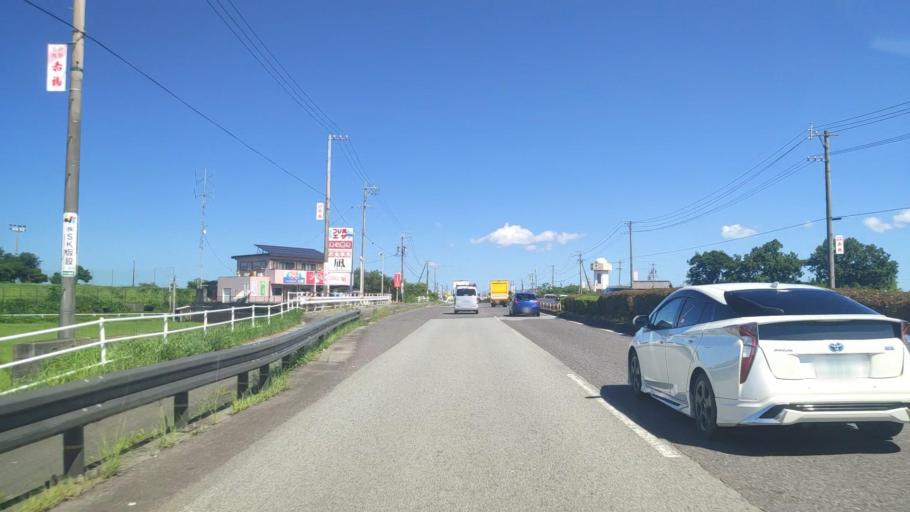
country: JP
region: Mie
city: Hisai-motomachi
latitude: 34.6029
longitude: 136.5253
